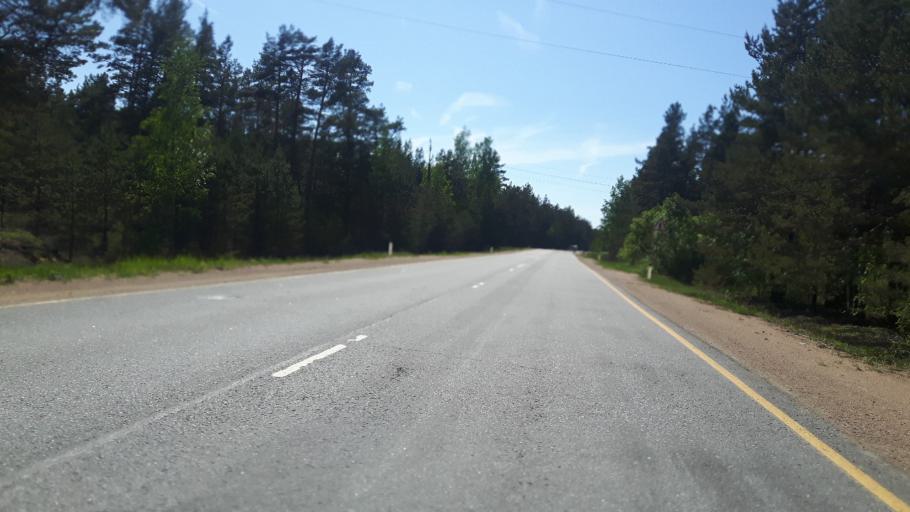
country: RU
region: Leningrad
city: Sista-Palkino
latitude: 59.7676
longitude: 28.7549
